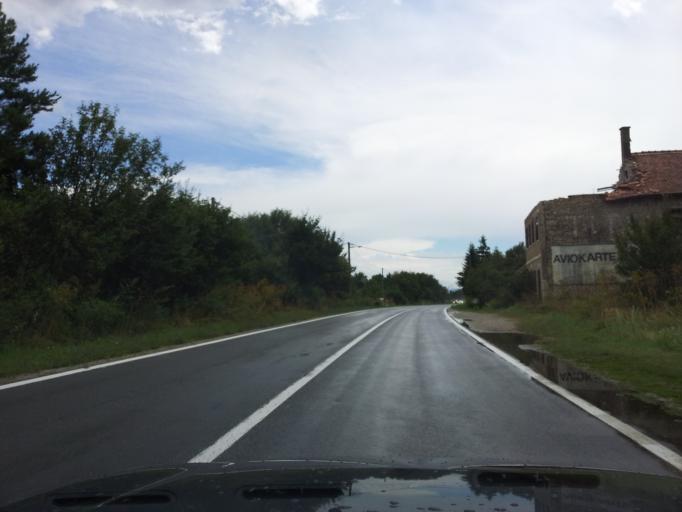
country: BA
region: Federation of Bosnia and Herzegovina
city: Bihac
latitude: 44.6448
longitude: 15.7208
